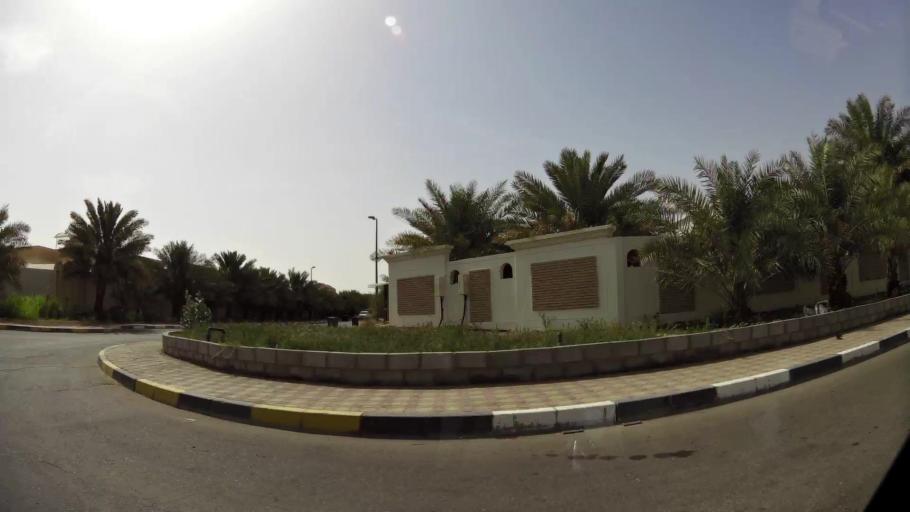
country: AE
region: Abu Dhabi
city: Al Ain
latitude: 24.1618
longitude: 55.6979
